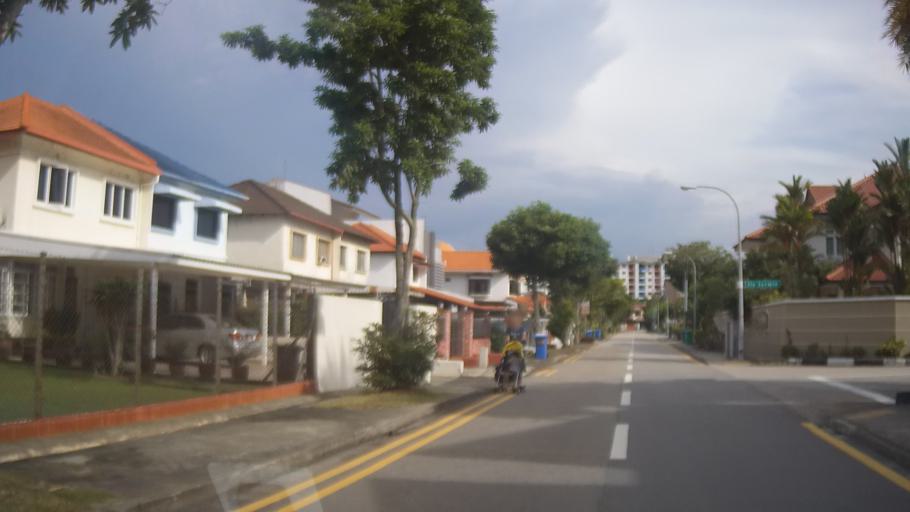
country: SG
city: Singapore
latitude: 1.3307
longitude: 103.8837
